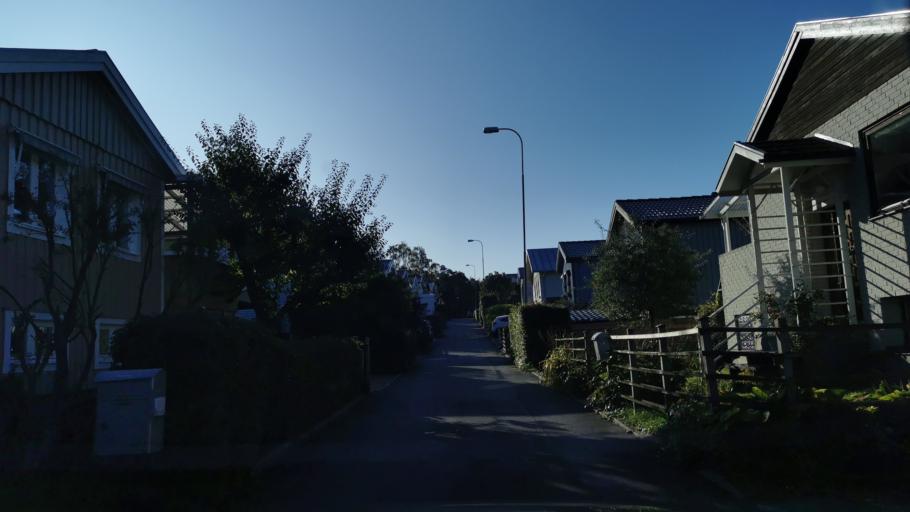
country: SE
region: Vaestra Goetaland
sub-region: Goteborg
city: Eriksbo
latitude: 57.7260
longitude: 12.0532
